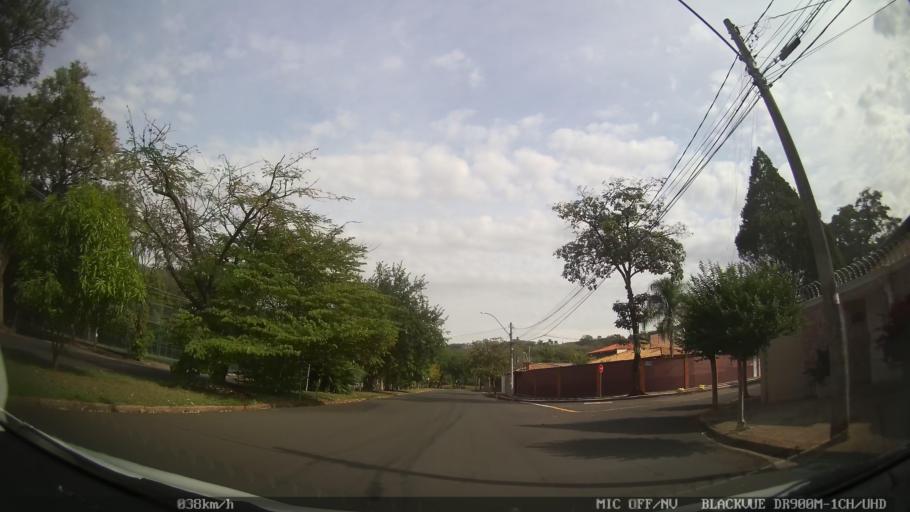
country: BR
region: Sao Paulo
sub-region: Piracicaba
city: Piracicaba
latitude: -22.7180
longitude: -47.6736
